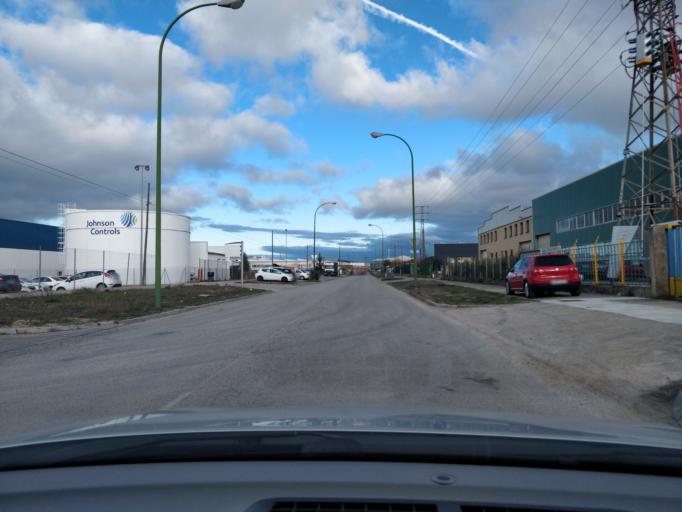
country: ES
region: Castille and Leon
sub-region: Provincia de Burgos
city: Villalbilla de Burgos
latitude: 42.3584
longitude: -3.7616
